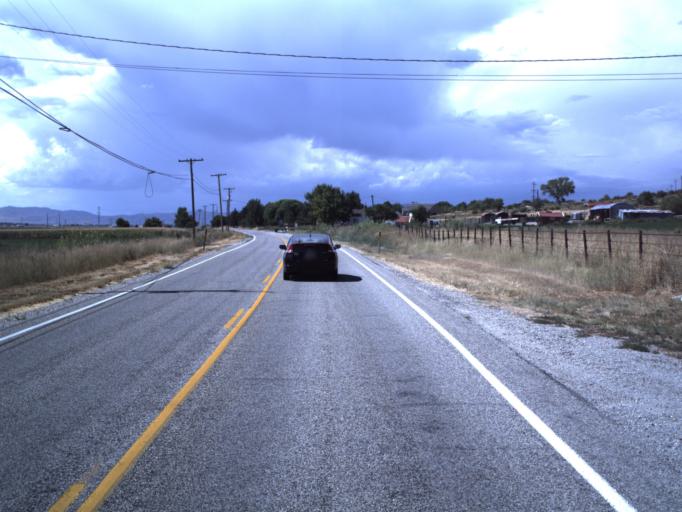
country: US
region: Utah
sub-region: Box Elder County
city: Honeyville
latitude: 41.5996
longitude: -112.0491
